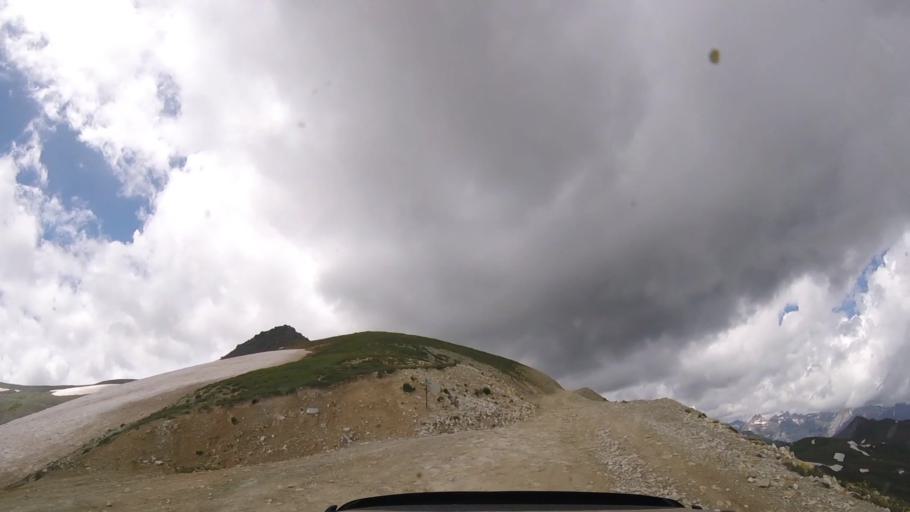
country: US
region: Colorado
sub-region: Ouray County
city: Ouray
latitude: 37.9733
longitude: -107.5861
